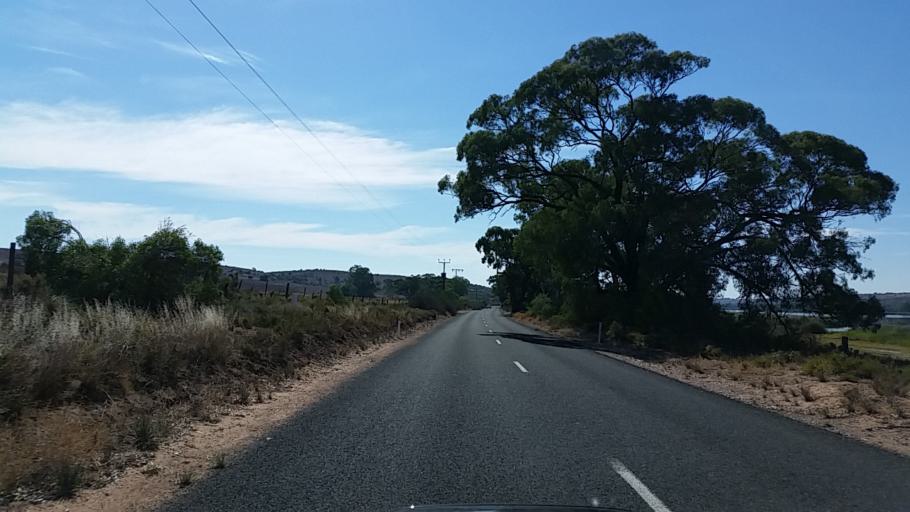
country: AU
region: South Australia
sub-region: Mid Murray
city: Mannum
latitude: -34.7240
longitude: 139.5446
